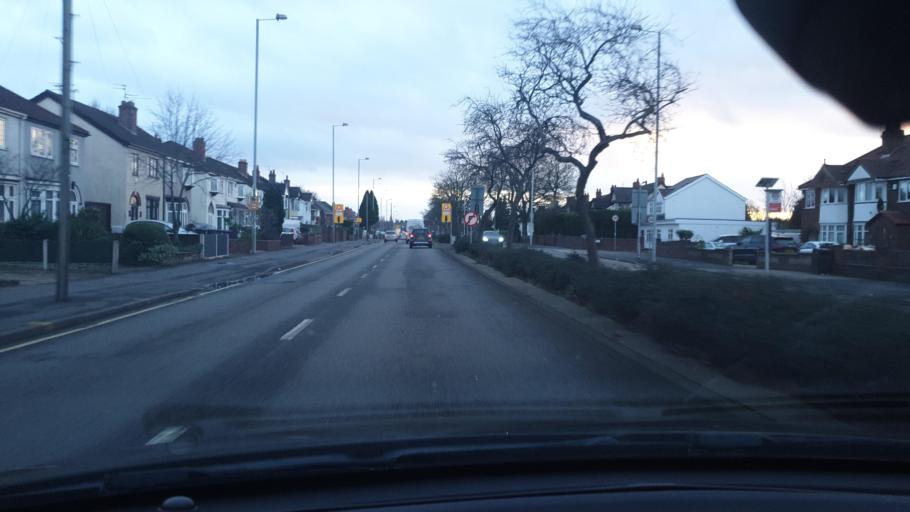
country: GB
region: England
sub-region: Wolverhampton
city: Wolverhampton
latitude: 52.6248
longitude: -2.1279
